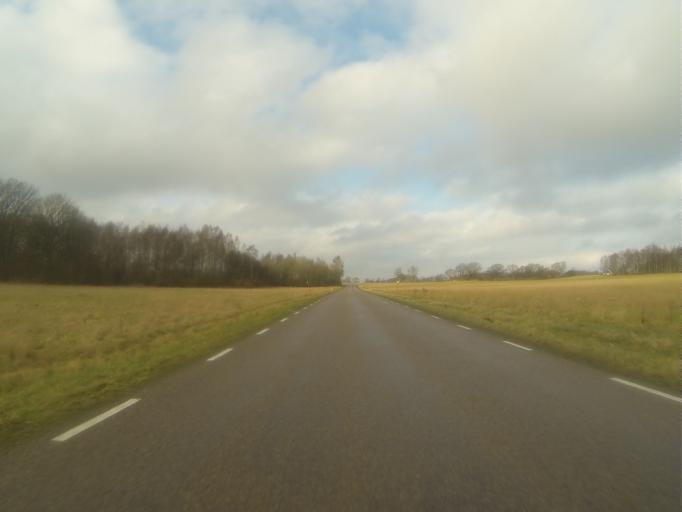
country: SE
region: Skane
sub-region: Svedala Kommun
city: Klagerup
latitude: 55.5646
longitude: 13.3146
